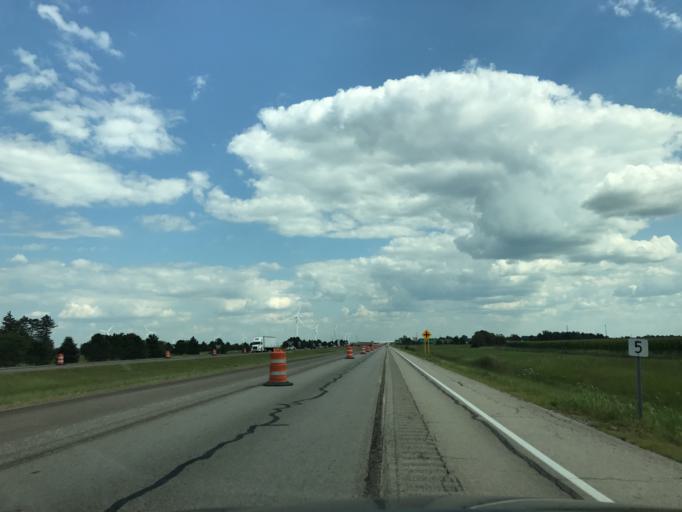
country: US
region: Ohio
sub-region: Van Wert County
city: Convoy
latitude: 40.9428
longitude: -84.7115
